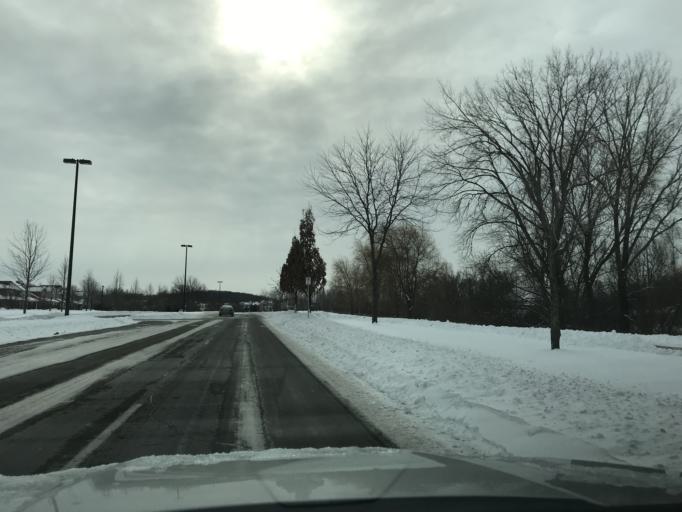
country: US
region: Wisconsin
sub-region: Dane County
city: Sun Prairie
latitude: 43.1600
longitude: -89.2638
